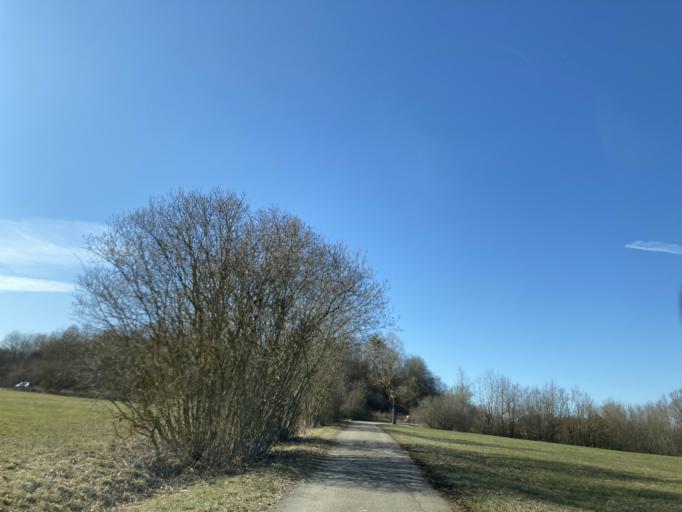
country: DE
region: Baden-Wuerttemberg
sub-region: Tuebingen Region
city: Bodelshausen
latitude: 48.3857
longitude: 8.9984
